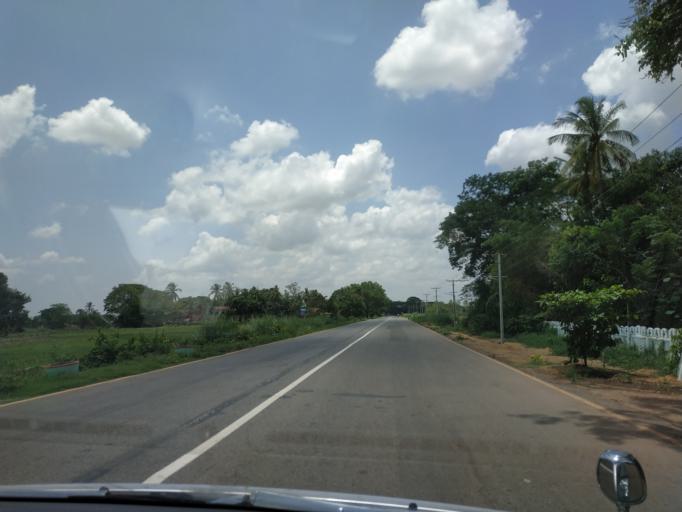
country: MM
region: Bago
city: Thanatpin
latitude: 17.4895
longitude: 96.6835
